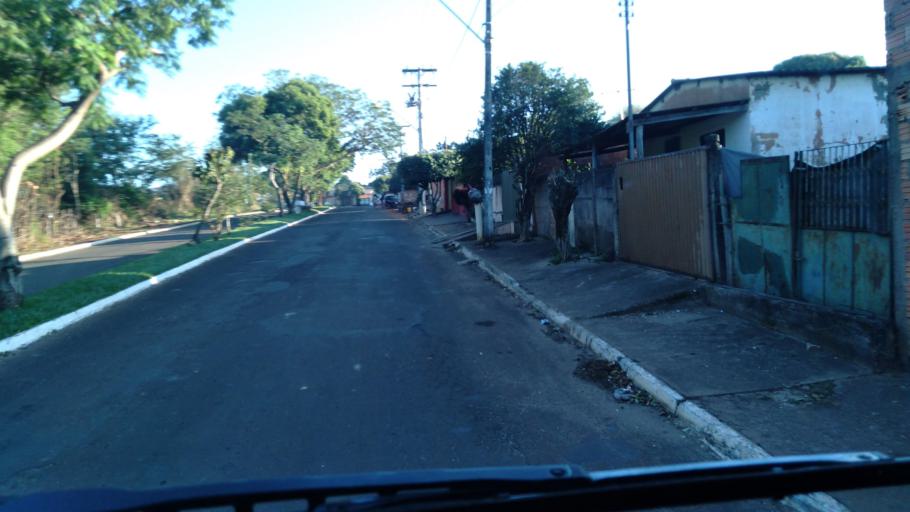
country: BR
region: Goias
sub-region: Mineiros
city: Mineiros
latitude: -17.5760
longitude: -52.5666
